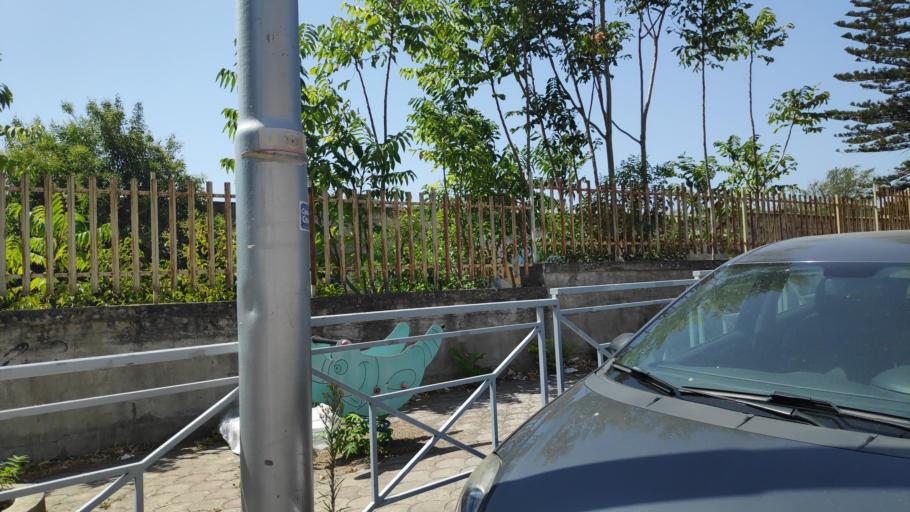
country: IT
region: Calabria
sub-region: Provincia di Catanzaro
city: Catanzaro
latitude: 38.8918
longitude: 16.6016
